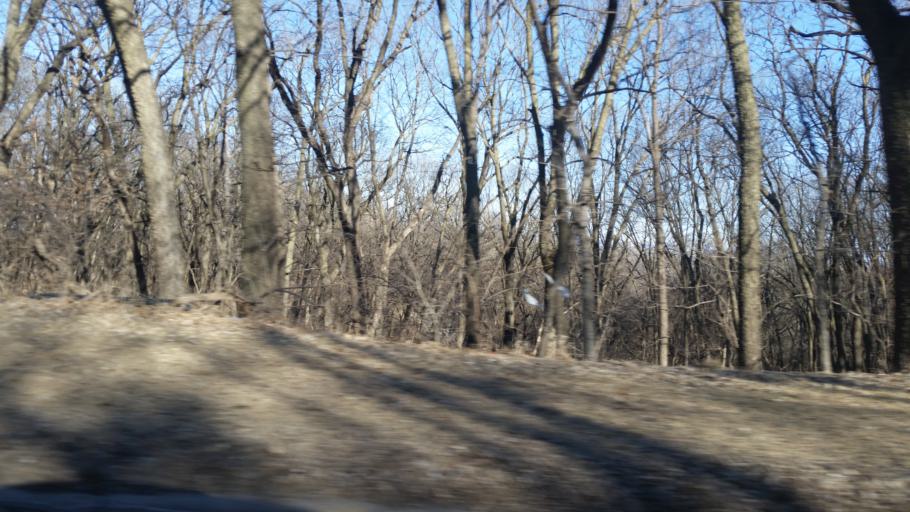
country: US
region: Nebraska
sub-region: Douglas County
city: Omaha
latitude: 41.1953
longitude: -95.9335
